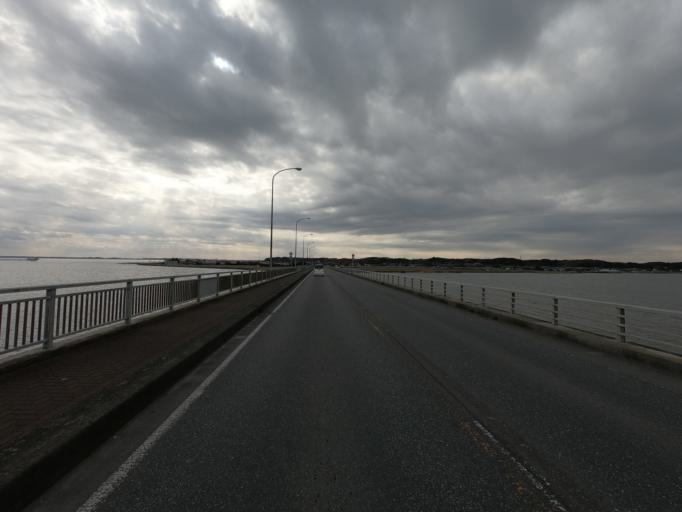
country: JP
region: Ibaraki
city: Inashiki
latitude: 36.0909
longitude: 140.3964
